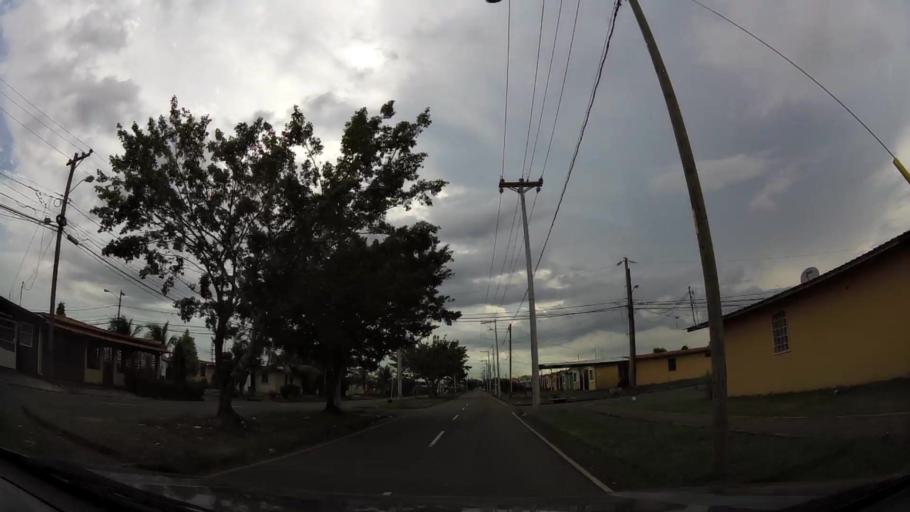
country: PA
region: Panama
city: Cabra Numero Uno
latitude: 9.0900
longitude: -79.3473
